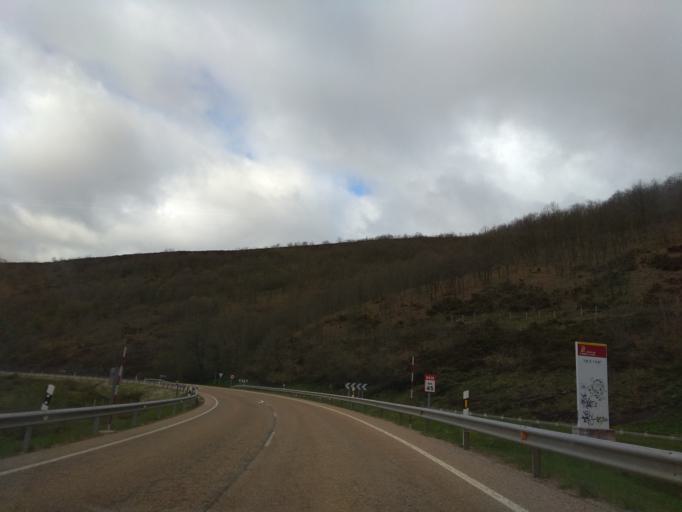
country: ES
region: Castille and Leon
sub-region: Provincia de Burgos
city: Espinosa de los Monteros
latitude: 43.1092
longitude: -3.4588
